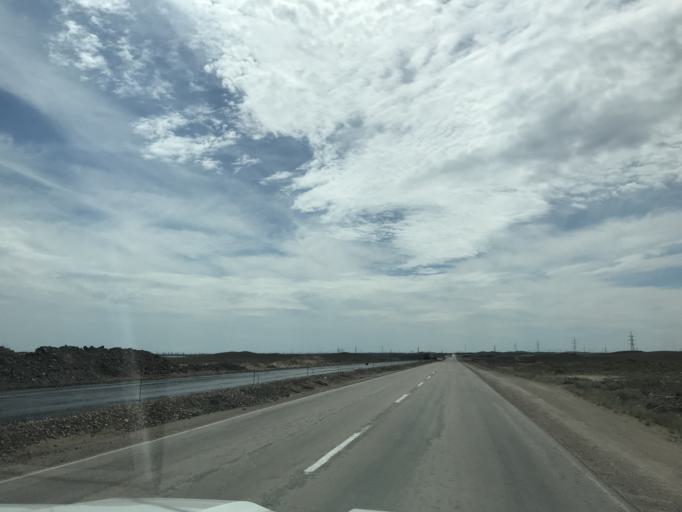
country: KZ
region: Almaty Oblysy
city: Ulken
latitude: 45.2248
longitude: 73.8531
